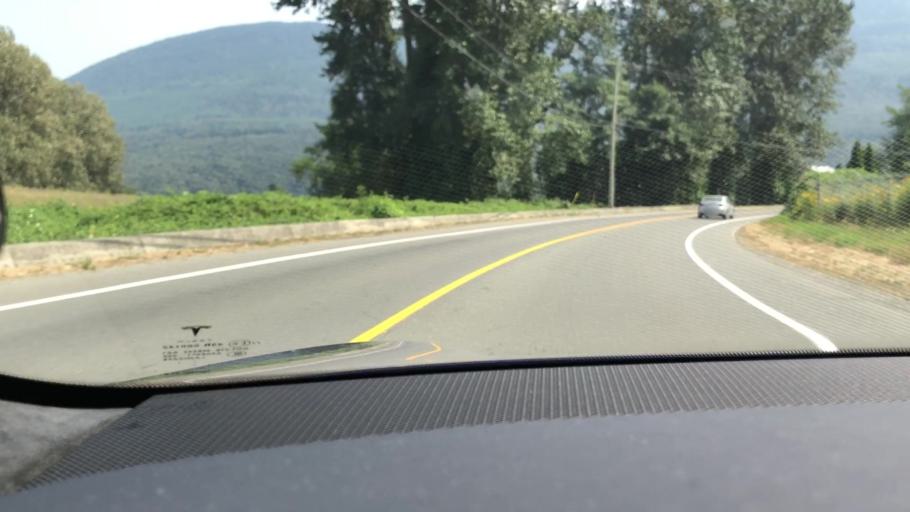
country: CA
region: British Columbia
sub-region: Fraser Valley Regional District
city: Chilliwack
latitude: 49.0887
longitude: -122.0653
